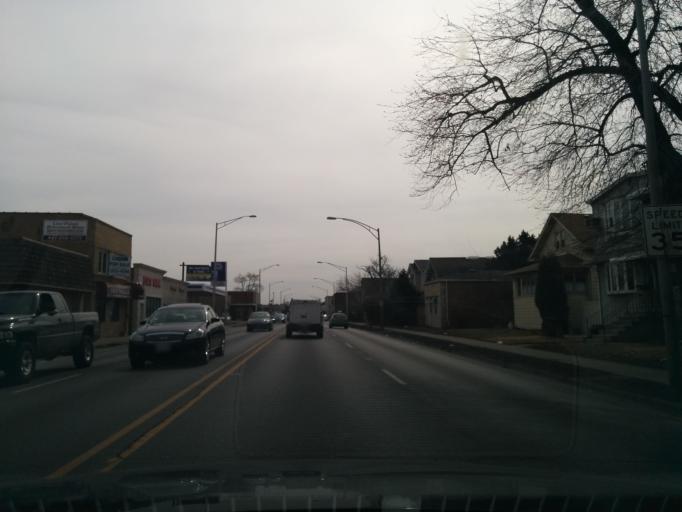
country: US
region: Illinois
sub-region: Cook County
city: Berwyn
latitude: 41.8613
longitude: -87.8041
